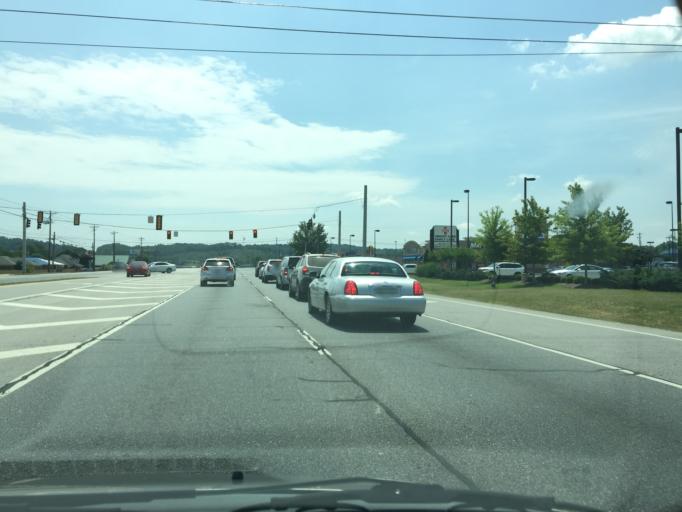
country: US
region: Georgia
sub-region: Catoosa County
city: Fort Oglethorpe
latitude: 34.9406
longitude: -85.2184
